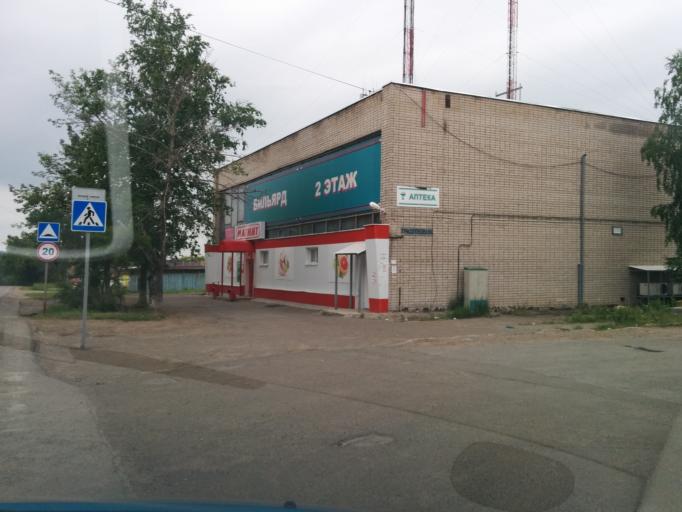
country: RU
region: Perm
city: Perm
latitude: 58.1616
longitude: 56.3053
